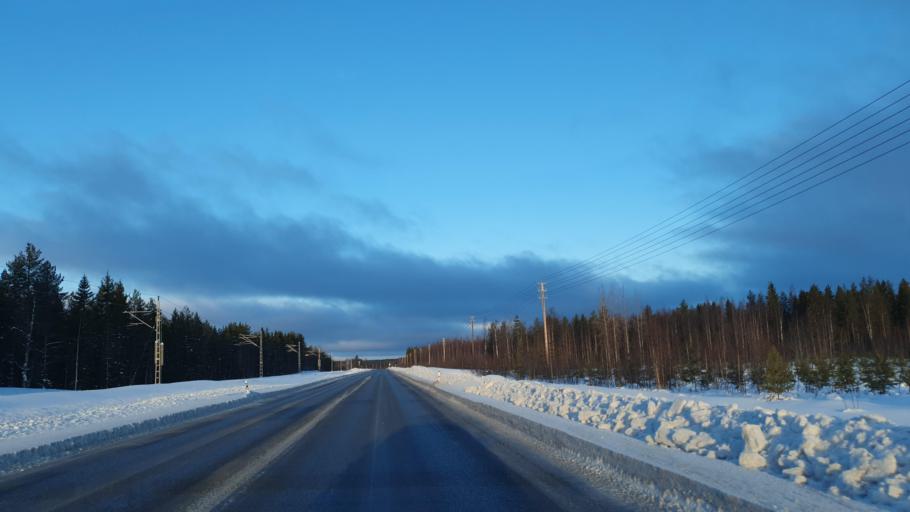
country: FI
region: Kainuu
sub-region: Kajaani
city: Paltamo
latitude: 64.4117
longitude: 27.7500
